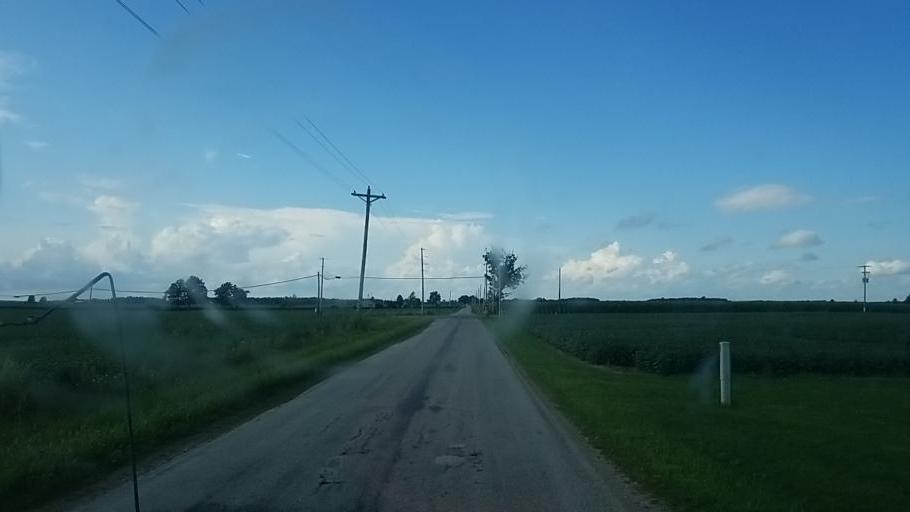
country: US
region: Ohio
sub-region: Hardin County
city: Forest
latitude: 40.8017
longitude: -83.3997
